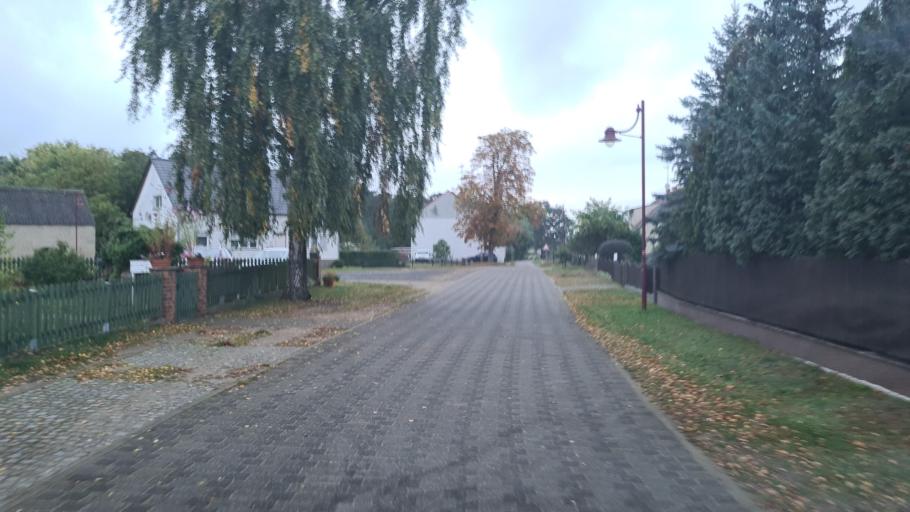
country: DE
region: Brandenburg
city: Munchehofe
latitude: 52.1631
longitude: 13.9197
